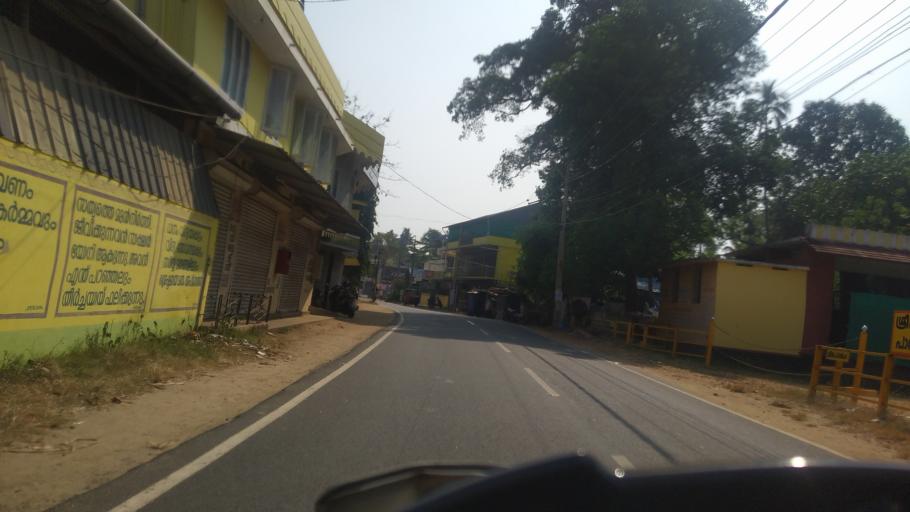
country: IN
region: Kerala
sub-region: Thrissur District
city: Kodungallur
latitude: 10.2081
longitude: 76.1854
